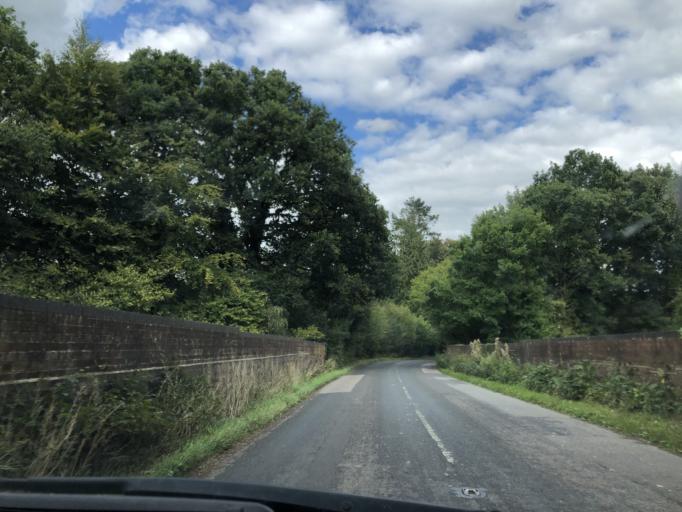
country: GB
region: England
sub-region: Kent
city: Sevenoaks
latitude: 51.1949
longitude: 0.1980
